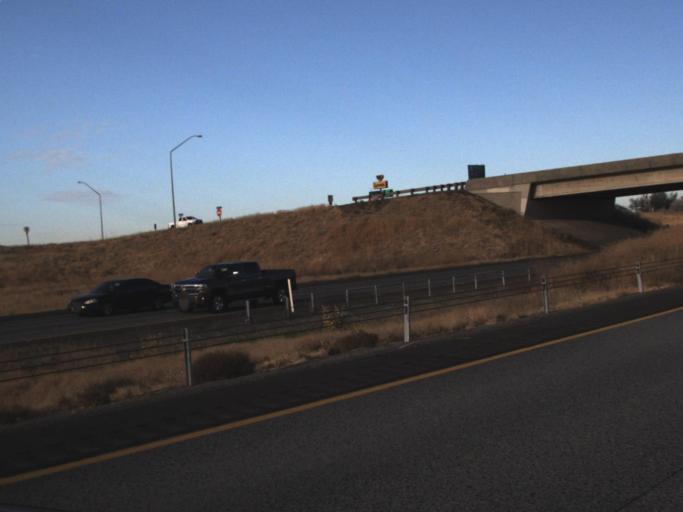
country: US
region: Washington
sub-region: Benton County
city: Prosser
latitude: 46.2223
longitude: -119.7895
